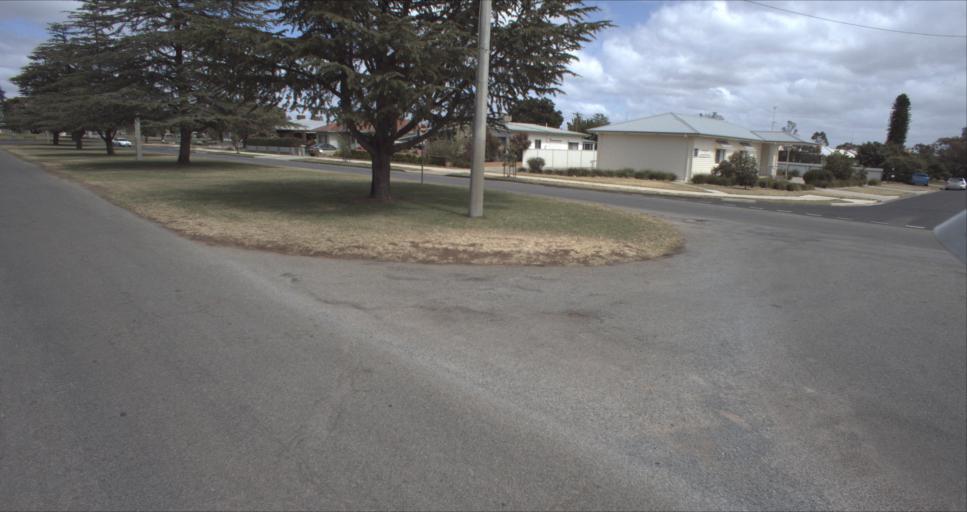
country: AU
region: New South Wales
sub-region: Leeton
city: Leeton
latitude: -34.5593
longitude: 146.3982
